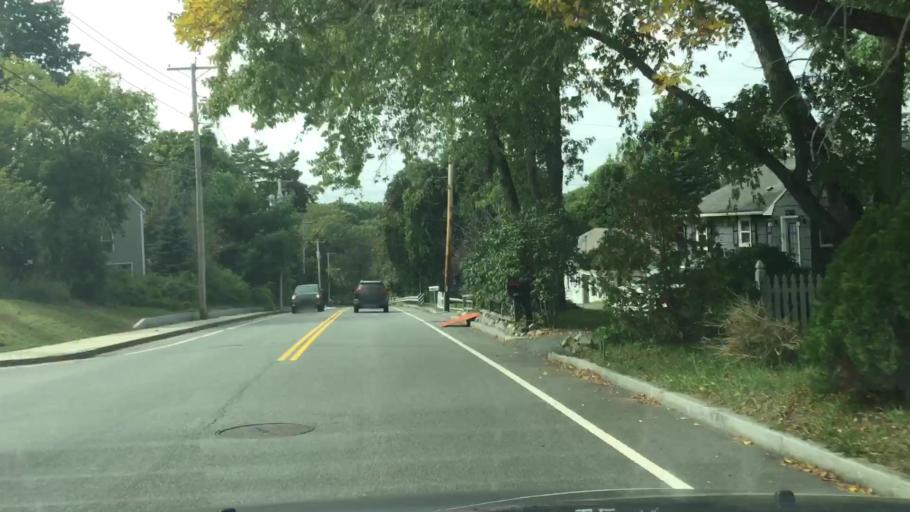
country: US
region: Massachusetts
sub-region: Middlesex County
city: Tewksbury
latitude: 42.6500
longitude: -71.2573
